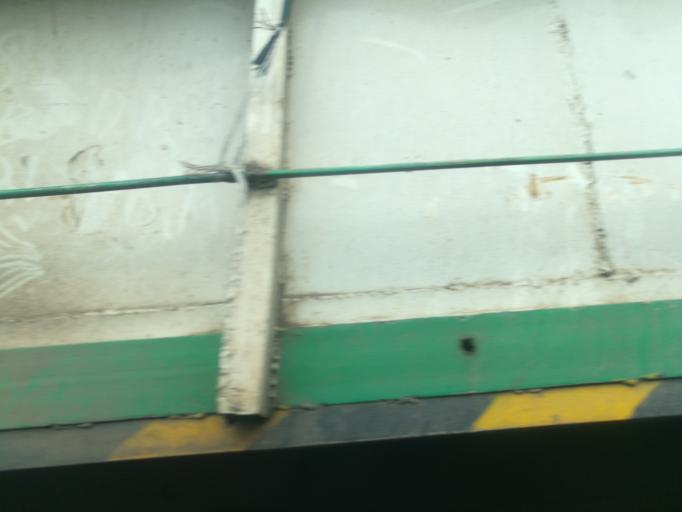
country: NG
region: Oyo
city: Ibadan
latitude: 7.3989
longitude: 3.9409
